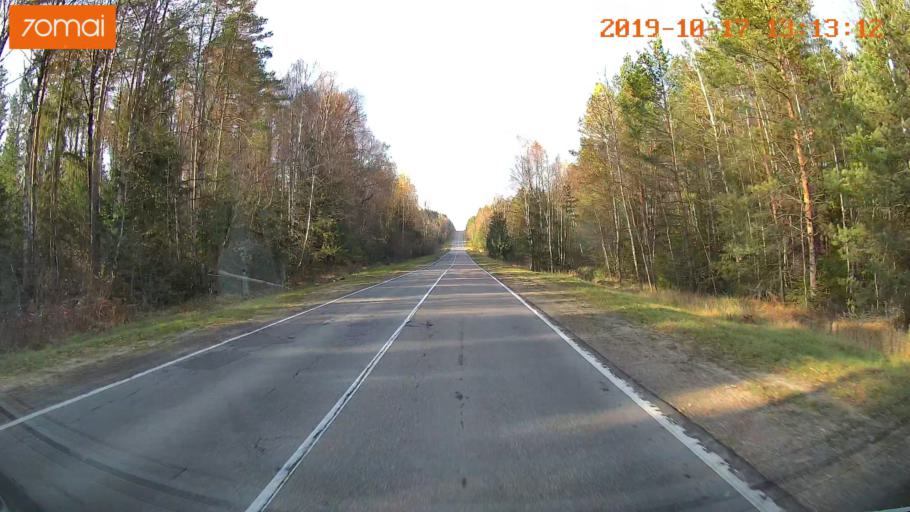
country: RU
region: Rjazan
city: Gus'-Zheleznyy
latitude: 55.0430
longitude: 41.1962
